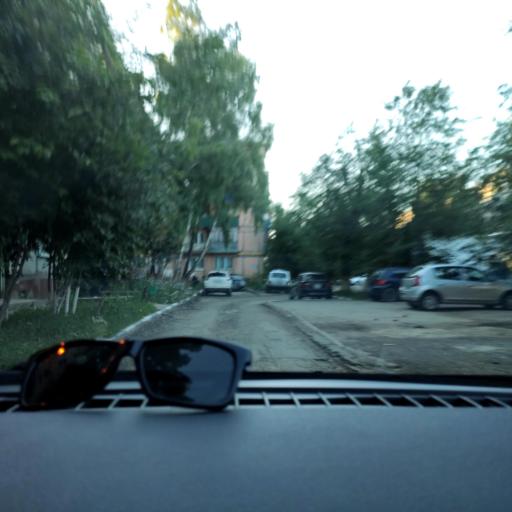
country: RU
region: Samara
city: Novokuybyshevsk
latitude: 53.0929
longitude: 49.9824
